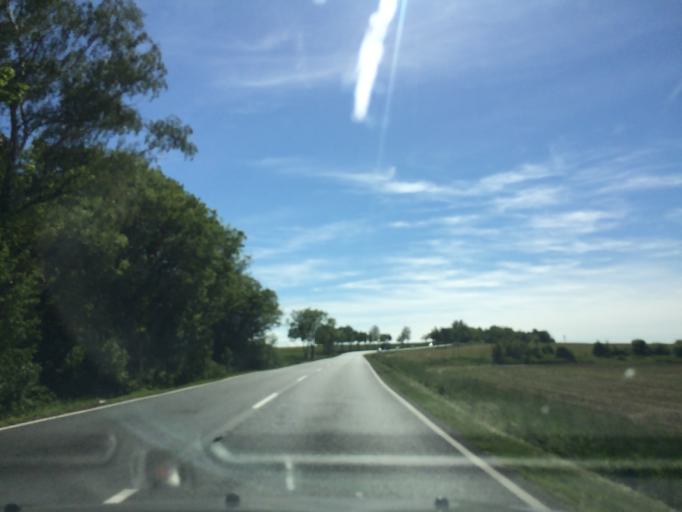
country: PL
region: Lower Silesian Voivodeship
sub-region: Powiat wroclawski
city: Sobotka
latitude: 50.9507
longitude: 16.7584
